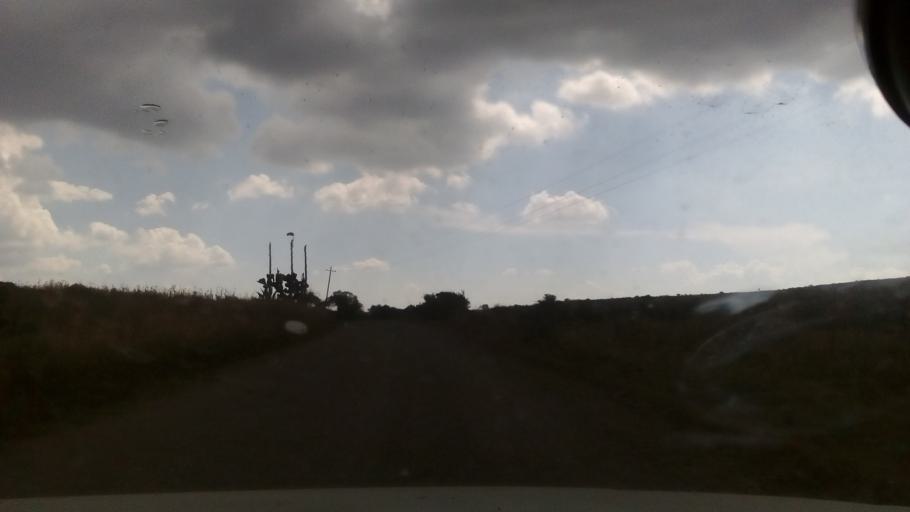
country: MX
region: Guanajuato
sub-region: Silao de la Victoria
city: San Francisco (Banos de Agua Caliente)
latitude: 21.1757
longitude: -101.4158
